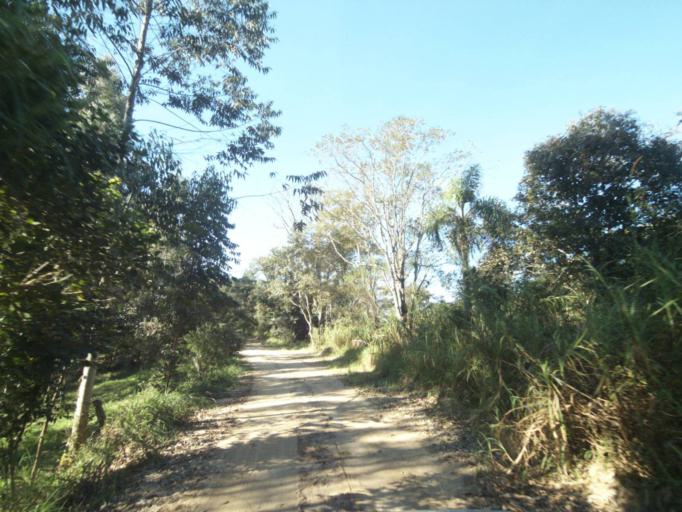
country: BR
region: Parana
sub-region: Tibagi
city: Tibagi
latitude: -24.5753
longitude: -50.4768
